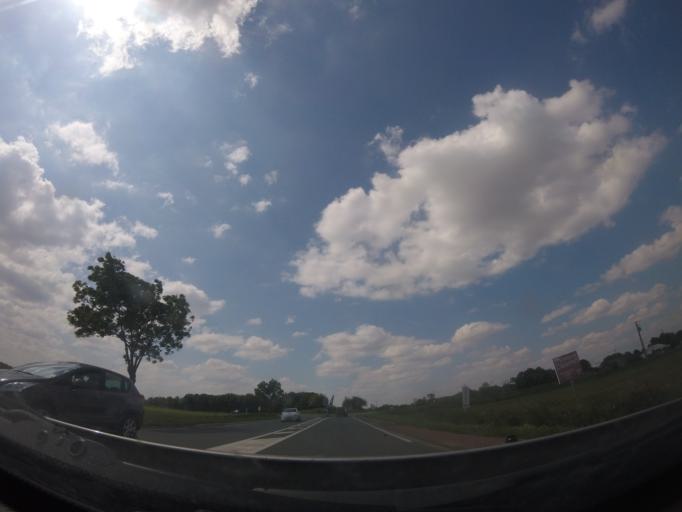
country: FR
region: Poitou-Charentes
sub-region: Departement de la Charente-Maritime
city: Saint-Porchaire
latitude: 45.8387
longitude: -0.8084
